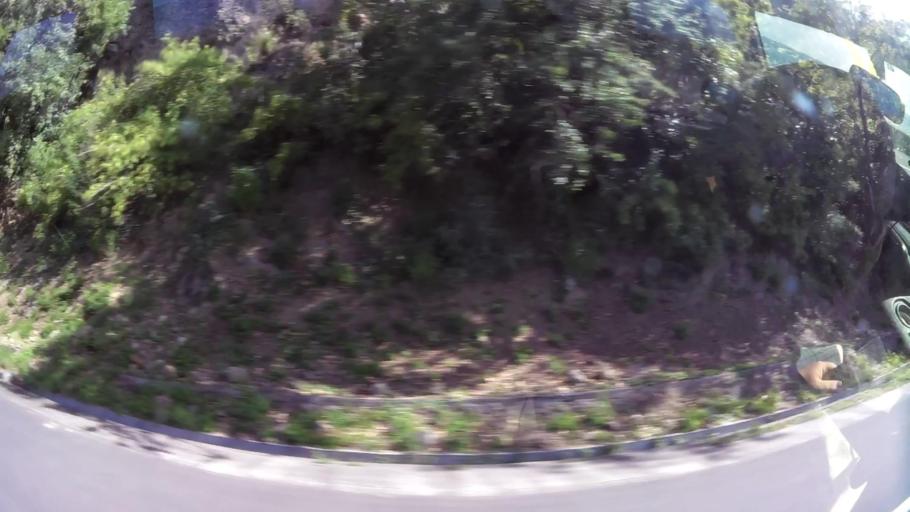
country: DM
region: Saint George
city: Roseau
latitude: 15.3216
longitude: -61.3946
